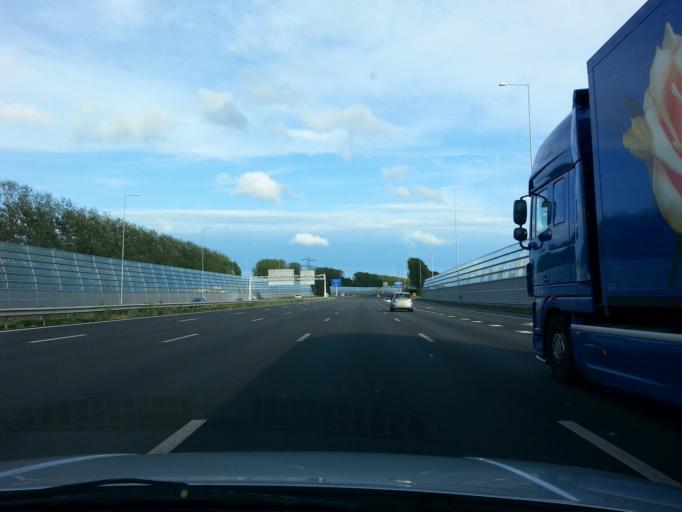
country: NL
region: North Holland
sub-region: Gemeente Diemen
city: Diemen
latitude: 52.3463
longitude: 4.9753
